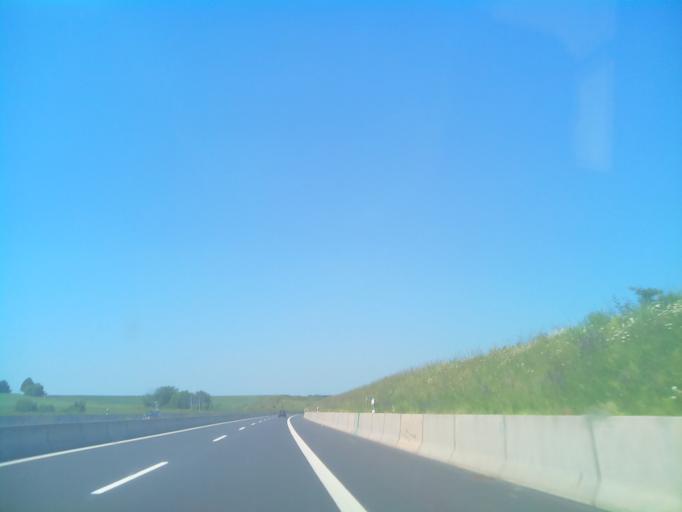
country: DE
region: Bavaria
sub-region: Regierungsbezirk Unterfranken
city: Munnerstadt
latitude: 50.2172
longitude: 10.2188
